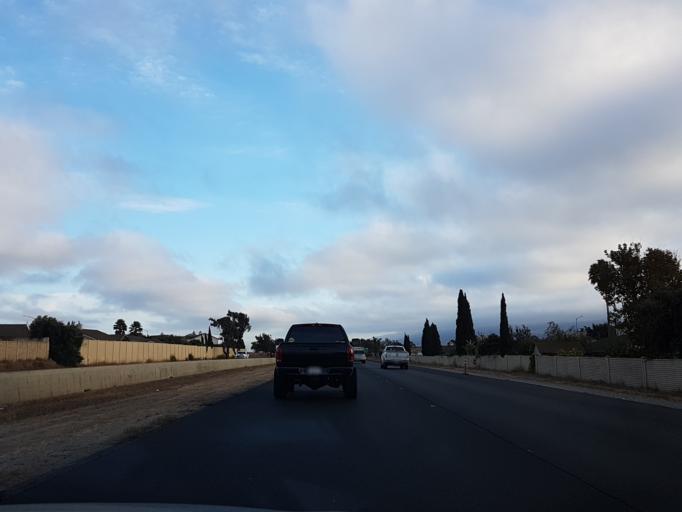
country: US
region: California
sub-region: Monterey County
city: Gonzales
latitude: 36.5085
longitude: -121.4353
